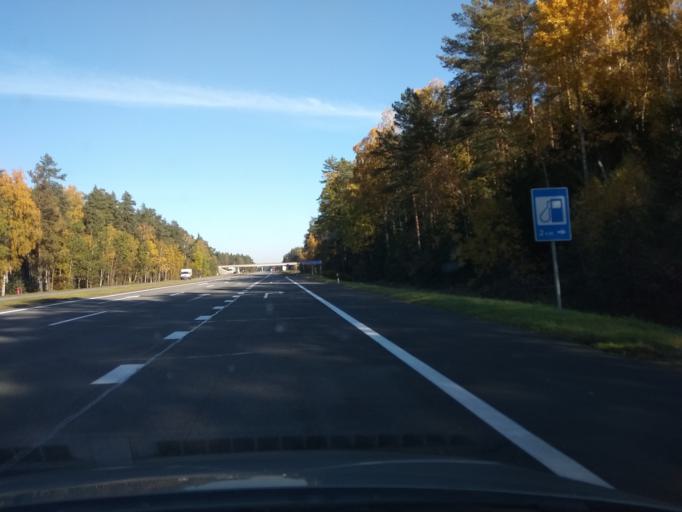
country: BY
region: Brest
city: Baranovichi
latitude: 53.0456
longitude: 25.8381
